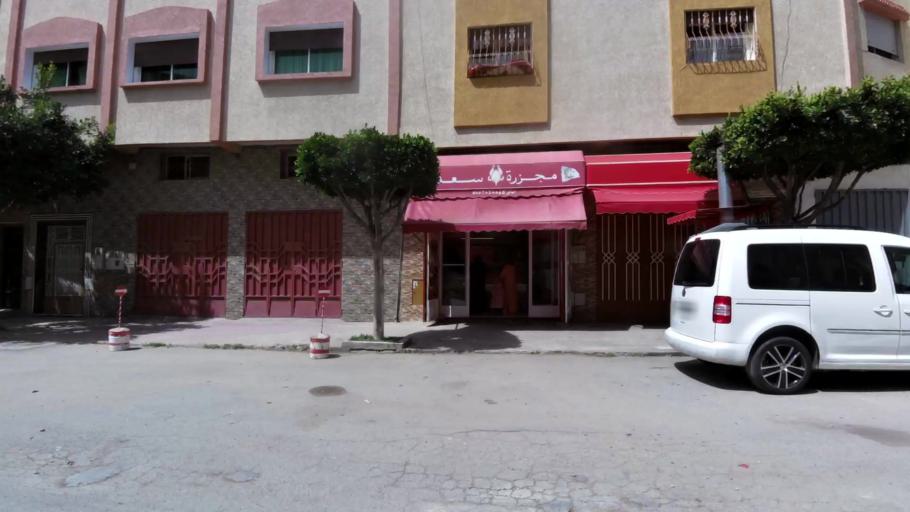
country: MA
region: Tanger-Tetouan
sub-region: Tanger-Assilah
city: Tangier
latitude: 35.7499
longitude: -5.8426
